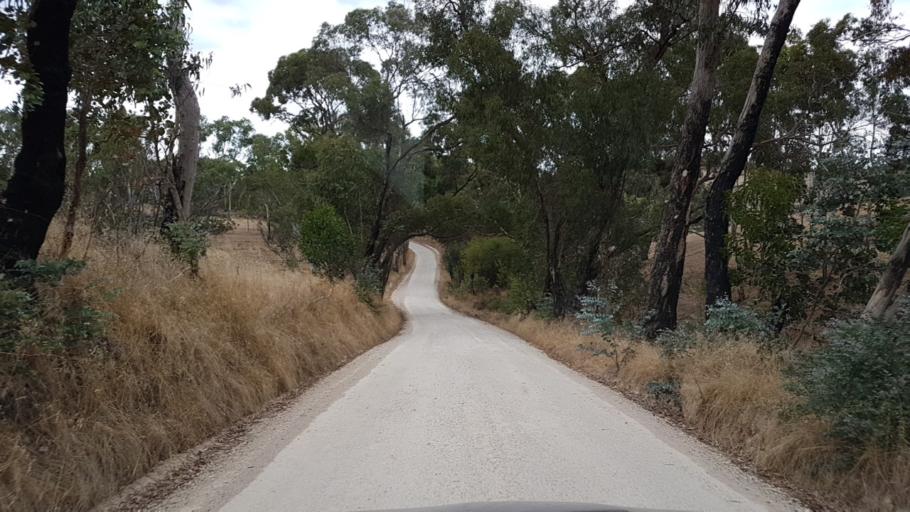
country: AU
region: South Australia
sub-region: Adelaide Hills
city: Gumeracha
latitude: -34.7995
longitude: 138.8337
